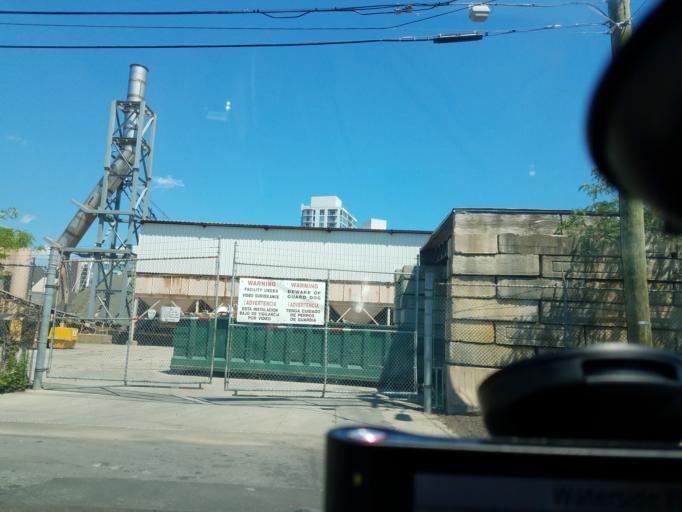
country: US
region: Connecticut
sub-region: Fairfield County
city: Stamford
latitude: 41.0402
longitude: -73.5469
